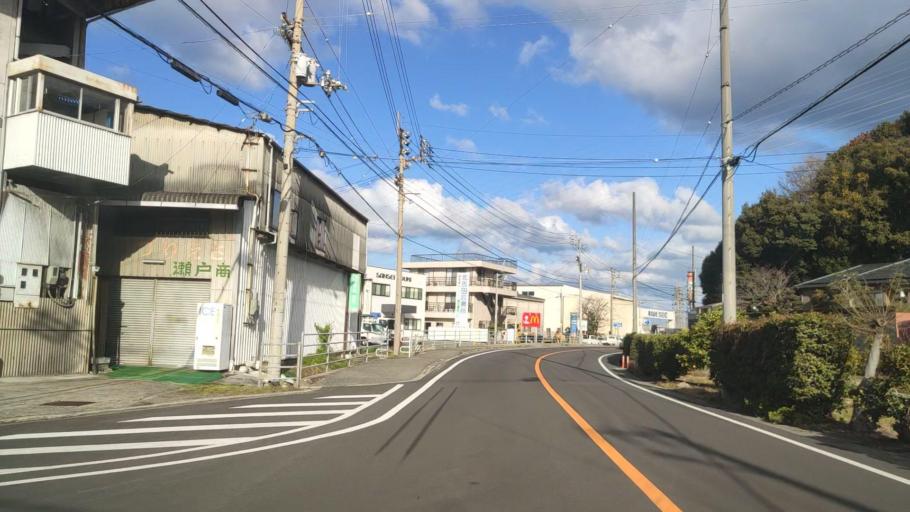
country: JP
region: Ehime
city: Masaki-cho
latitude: 33.8416
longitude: 132.7082
